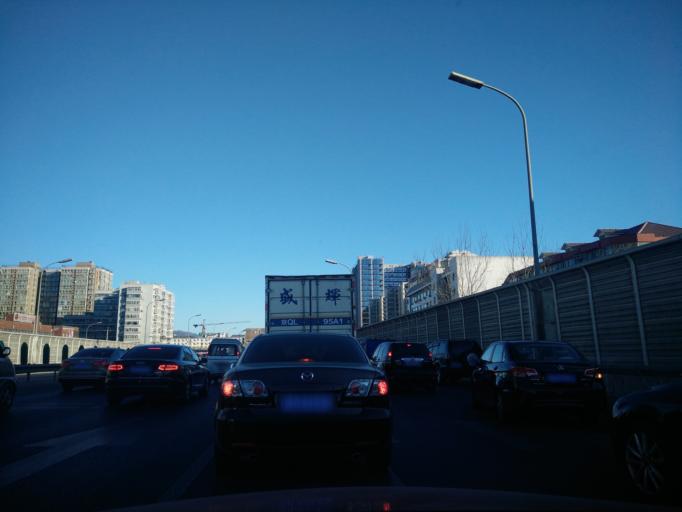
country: CN
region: Beijing
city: Lugu
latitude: 39.8978
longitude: 116.2052
